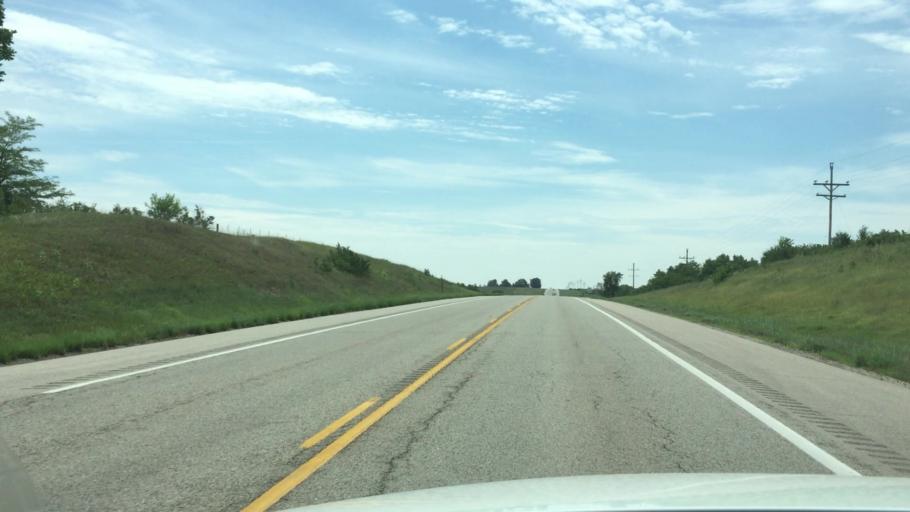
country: US
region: Kansas
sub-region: Nemaha County
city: Sabetha
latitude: 39.7974
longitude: -95.7294
